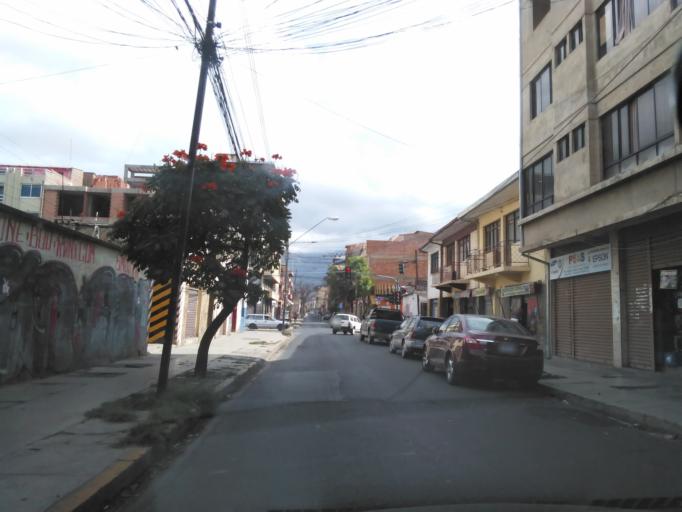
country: BO
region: Cochabamba
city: Cochabamba
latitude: -17.3960
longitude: -66.1515
